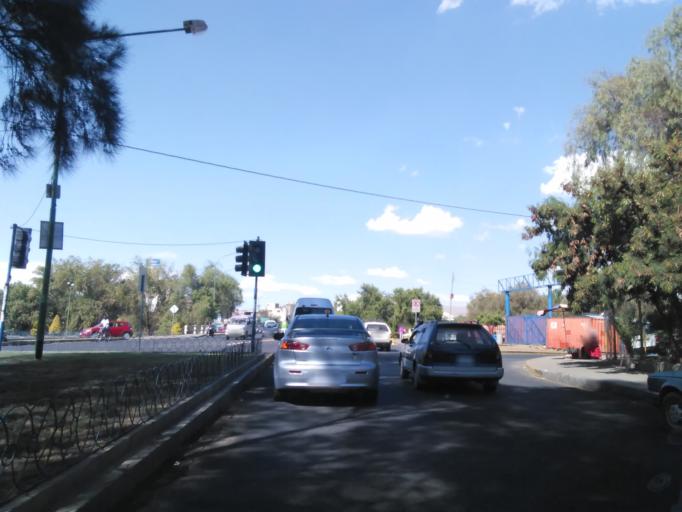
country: BO
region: Cochabamba
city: Cochabamba
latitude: -17.3967
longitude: -66.1686
